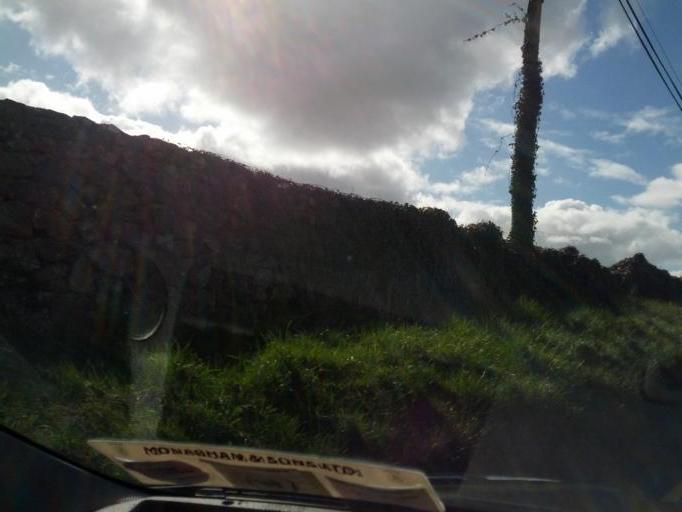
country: IE
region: Connaught
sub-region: County Galway
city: Athenry
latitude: 53.3861
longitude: -8.6869
